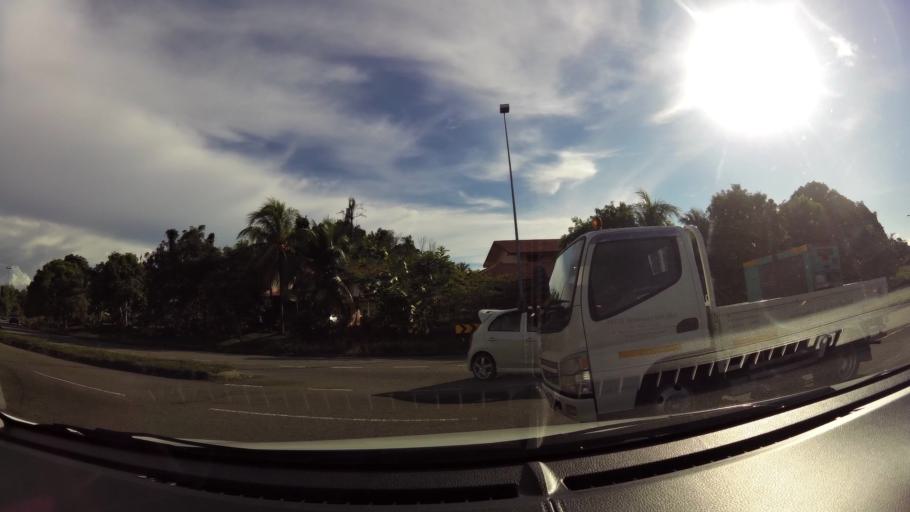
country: BN
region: Brunei and Muara
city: Bandar Seri Begawan
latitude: 4.9806
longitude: 114.9639
